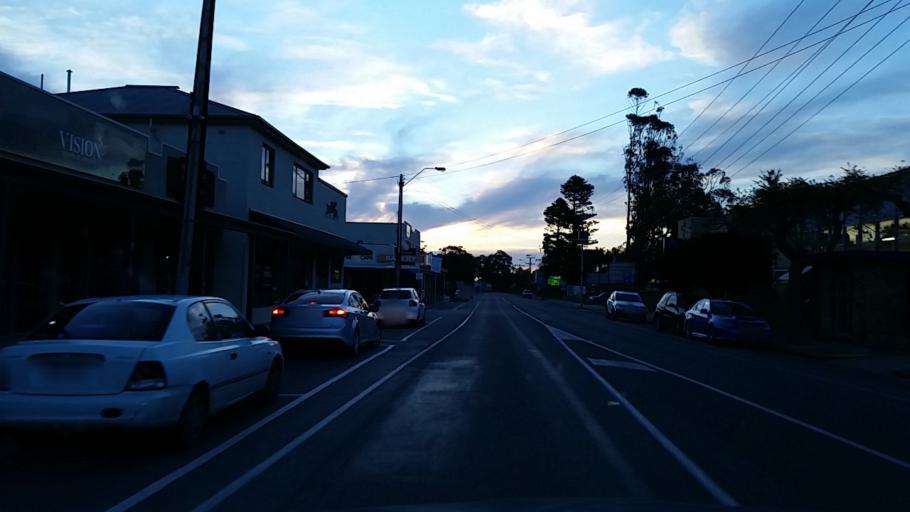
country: AU
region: South Australia
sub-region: Yankalilla
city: Normanville
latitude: -35.4574
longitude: 138.3498
